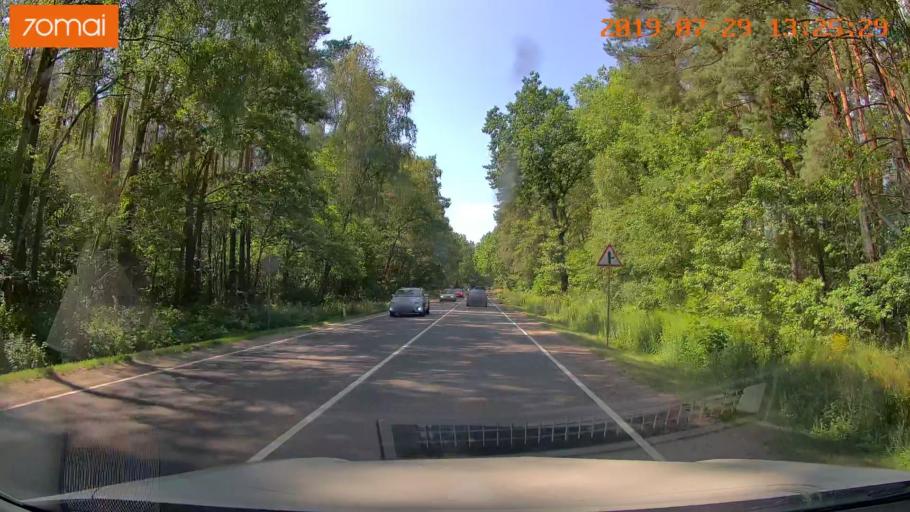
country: RU
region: Kaliningrad
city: Vzmorye
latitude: 54.7101
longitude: 20.3301
